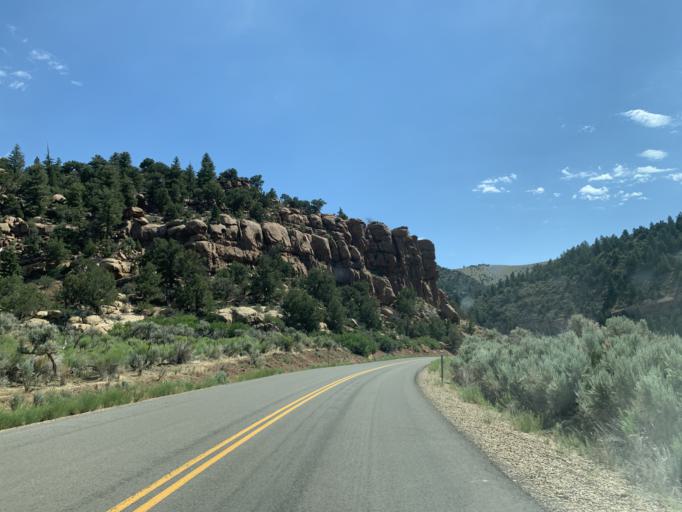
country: US
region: Utah
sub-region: Carbon County
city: East Carbon City
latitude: 39.7558
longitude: -110.5317
